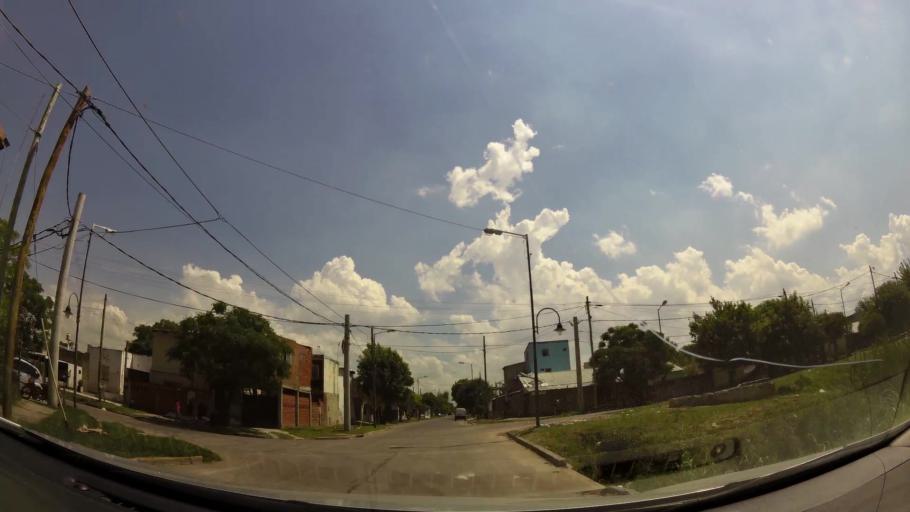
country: AR
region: Buenos Aires
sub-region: Partido de Tigre
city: Tigre
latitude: -34.4669
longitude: -58.5899
